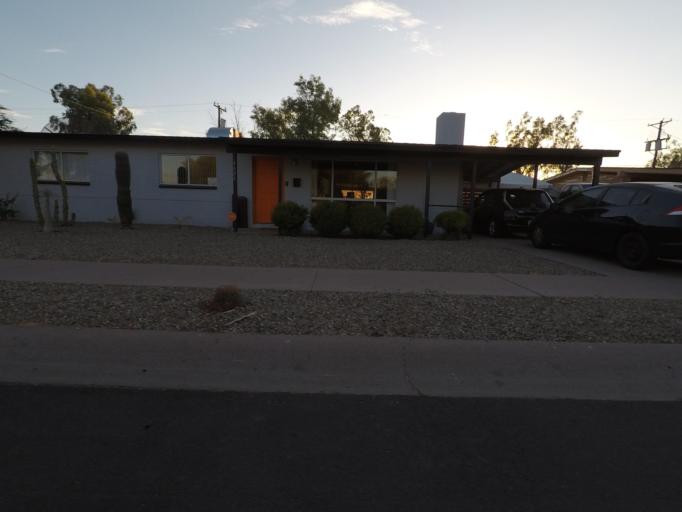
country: US
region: Arizona
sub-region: Maricopa County
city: Glendale
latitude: 33.5045
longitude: -112.1418
